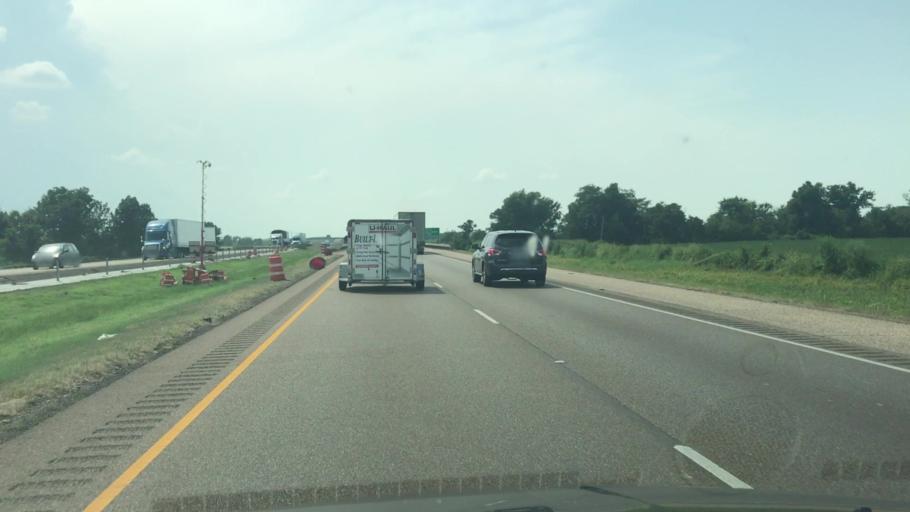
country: US
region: Arkansas
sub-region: Crittenden County
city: Earle
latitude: 35.1511
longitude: -90.3879
